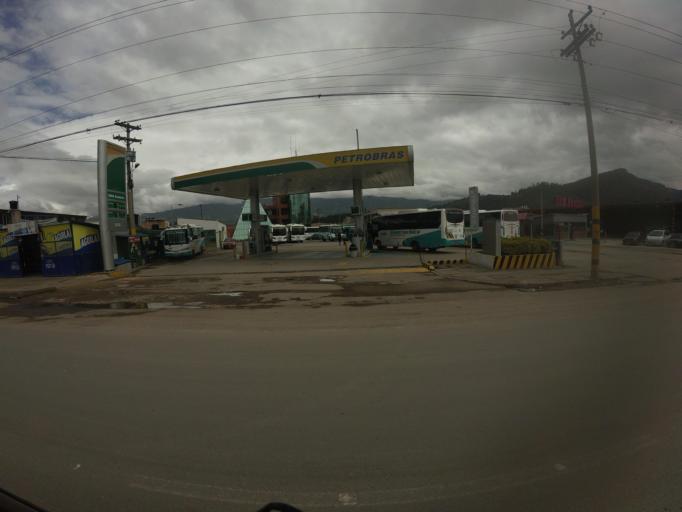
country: CO
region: Boyaca
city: Duitama
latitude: 5.8104
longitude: -73.0182
